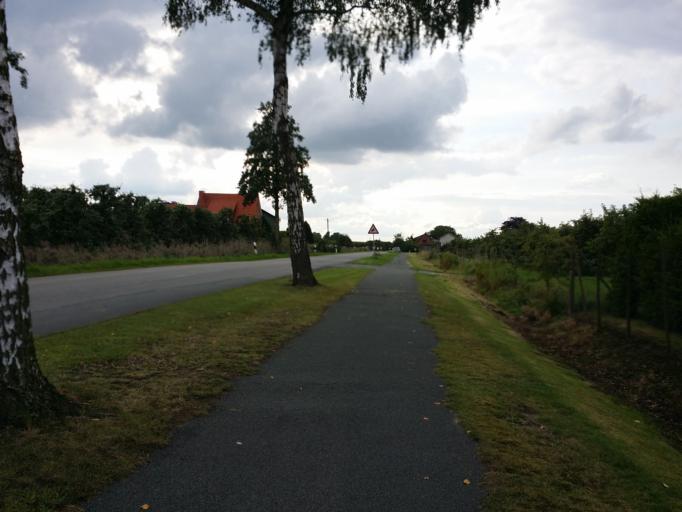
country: DE
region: Lower Saxony
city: Oederquart
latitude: 53.7848
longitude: 9.2316
